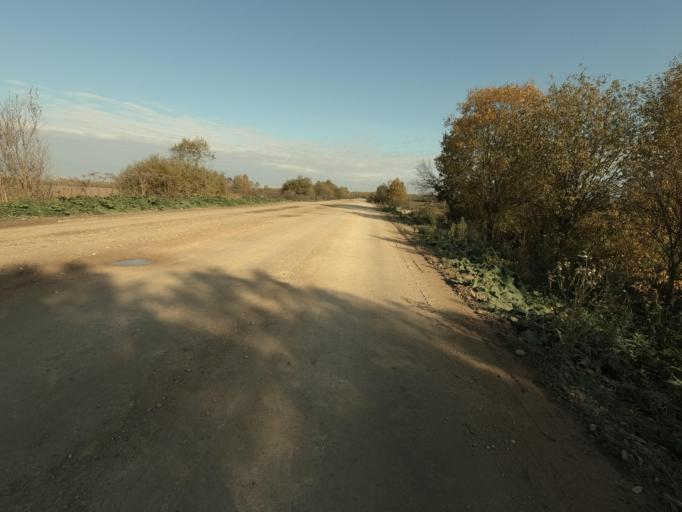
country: RU
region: Novgorod
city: Batetskiy
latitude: 58.8149
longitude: 30.6983
